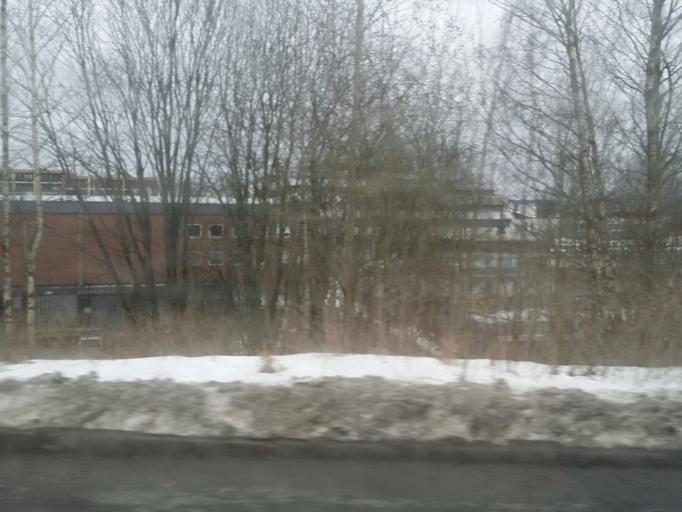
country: NO
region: Oslo
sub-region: Oslo
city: Oslo
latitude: 59.8965
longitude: 10.7995
